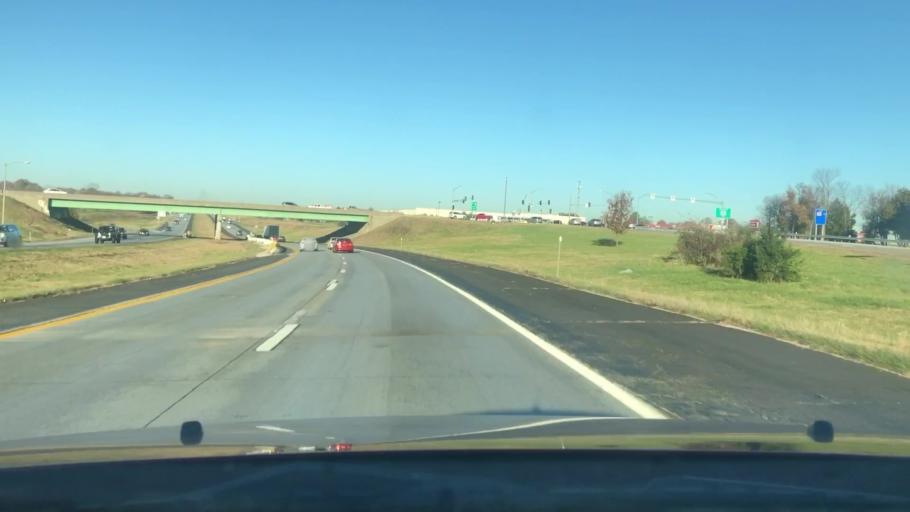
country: US
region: Missouri
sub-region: Greene County
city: Springfield
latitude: 37.1387
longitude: -93.2509
